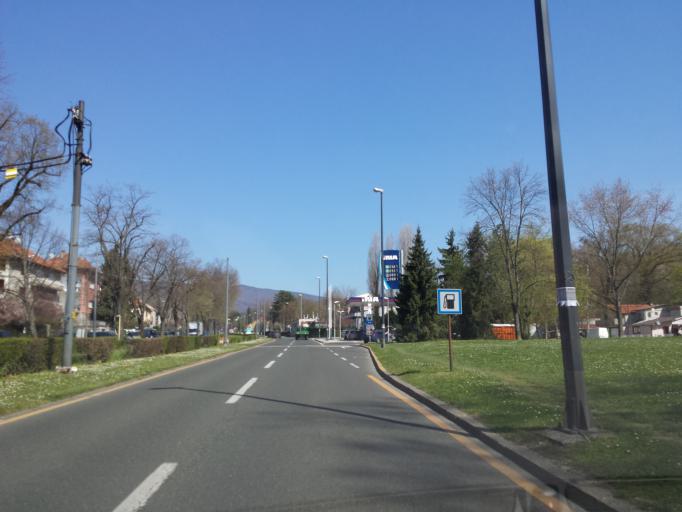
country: HR
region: Grad Zagreb
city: Zagreb
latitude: 45.8328
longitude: 15.9782
